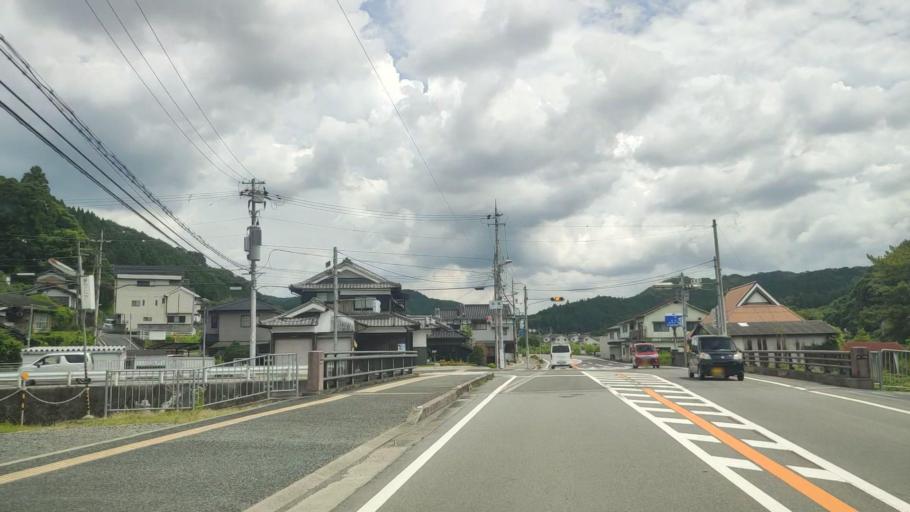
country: JP
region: Hyogo
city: Yamazakicho-nakabirose
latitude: 34.9827
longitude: 134.4389
